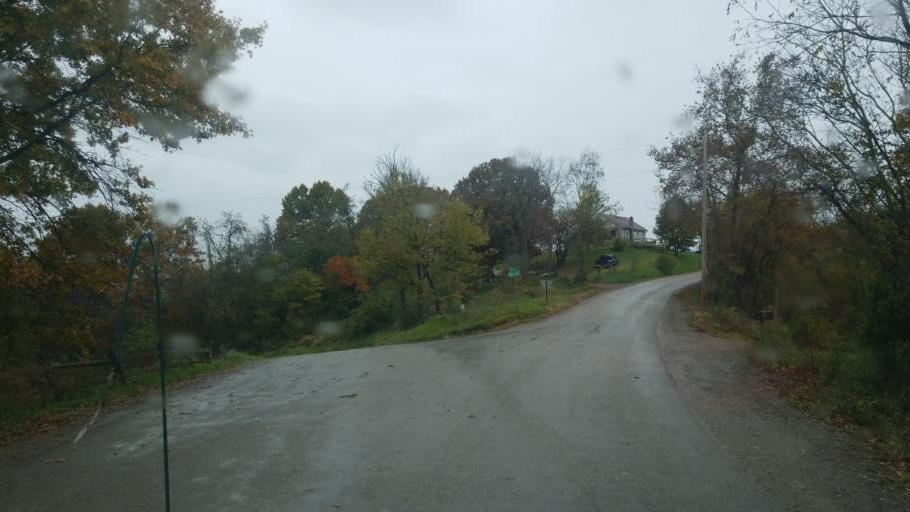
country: US
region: Ohio
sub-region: Washington County
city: Belpre
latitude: 39.3138
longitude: -81.5914
